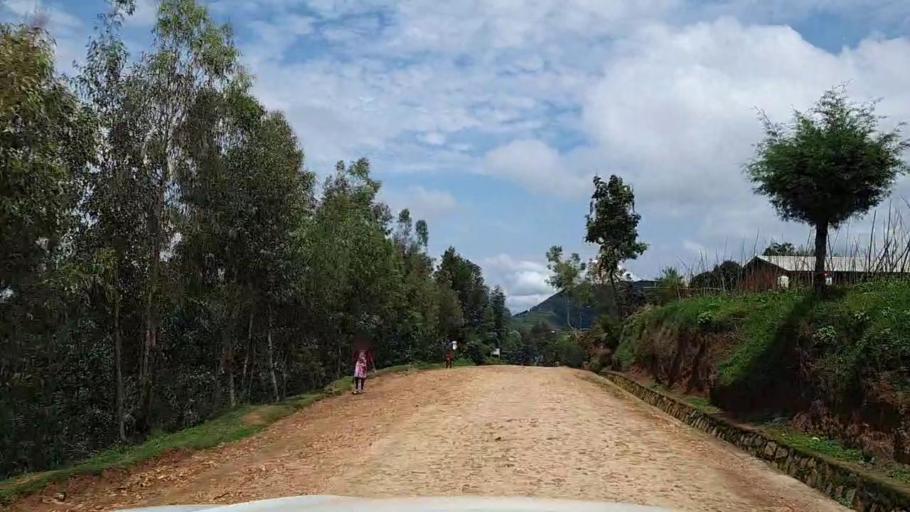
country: RW
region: Southern Province
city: Gikongoro
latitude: -2.3354
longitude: 29.5212
